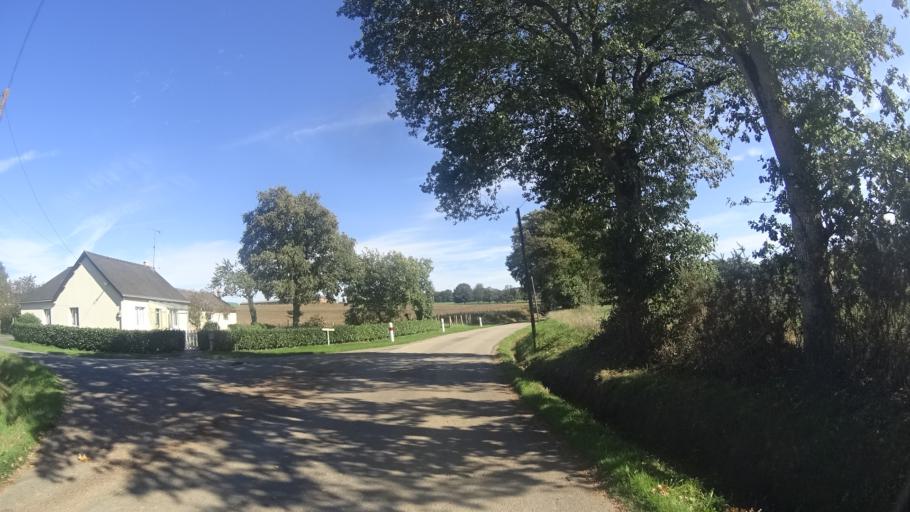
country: FR
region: Brittany
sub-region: Departement du Morbihan
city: Peillac
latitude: 47.7320
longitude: -2.1799
